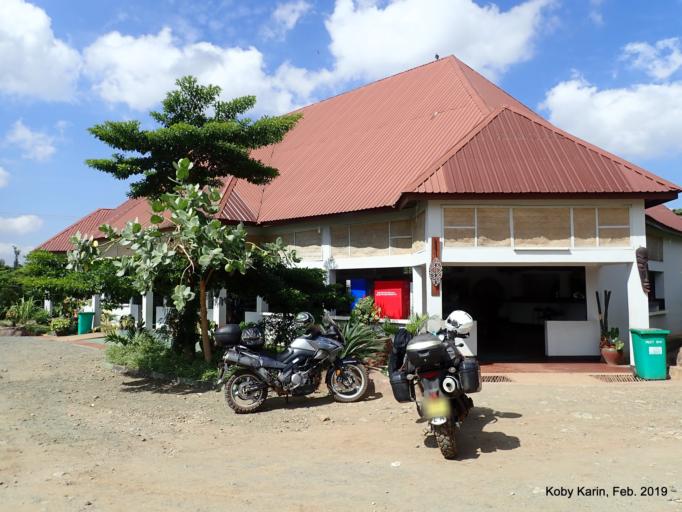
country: TZ
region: Manyara
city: Babati
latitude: -4.1878
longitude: 35.7535
